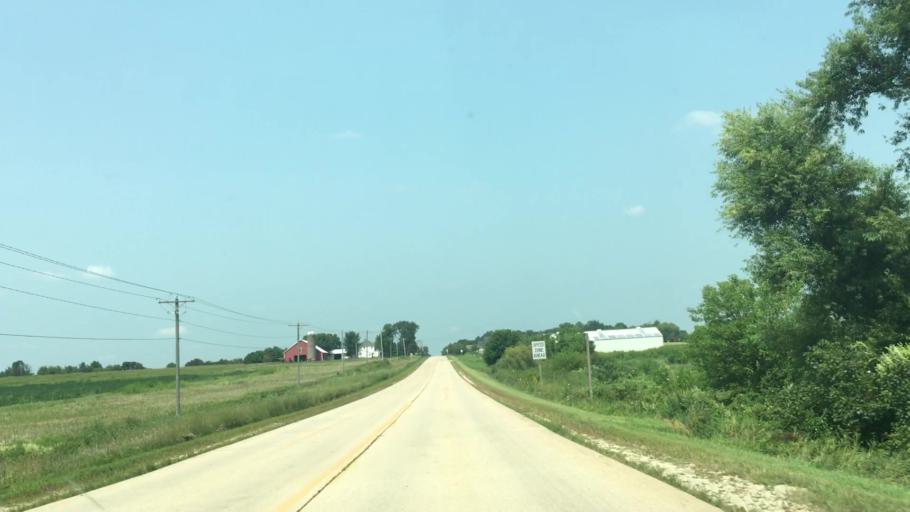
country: US
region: Iowa
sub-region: Fayette County
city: Oelwein
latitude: 42.6701
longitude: -91.8937
